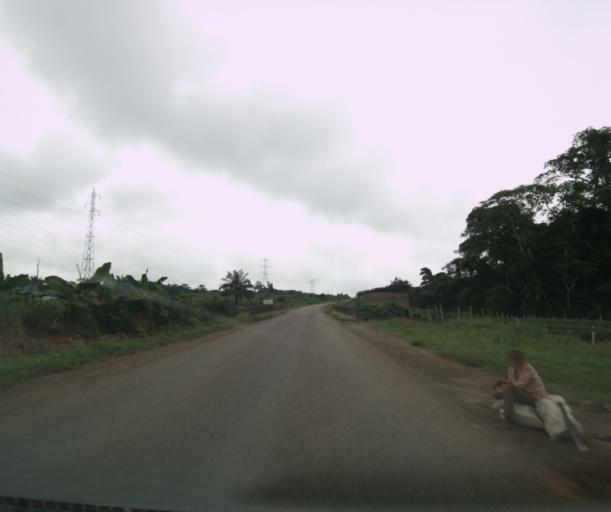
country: CM
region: Littoral
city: Edea
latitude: 3.6874
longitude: 10.1066
